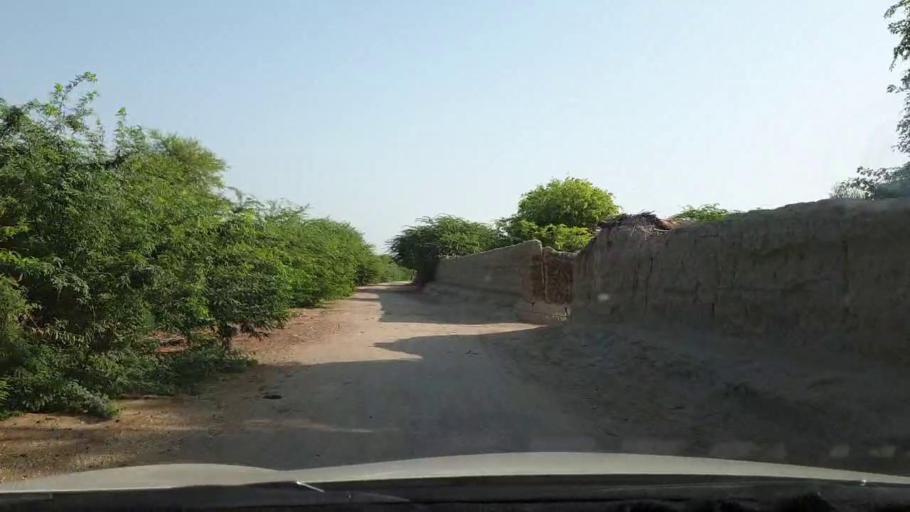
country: PK
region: Sindh
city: Larkana
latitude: 27.5568
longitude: 68.2570
